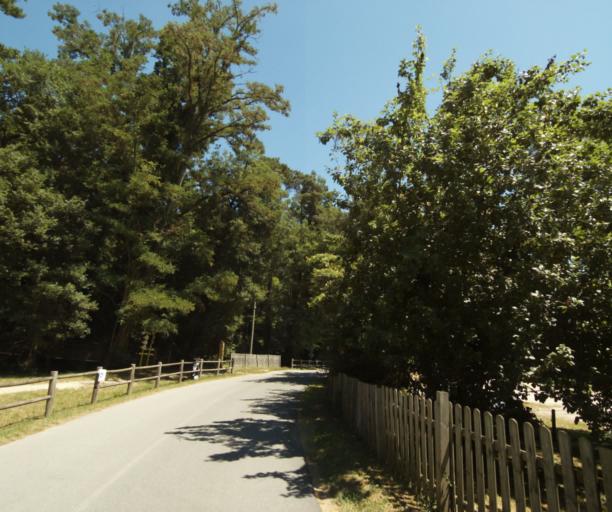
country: FR
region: Centre
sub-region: Departement du Loiret
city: Malesherbes
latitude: 48.2943
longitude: 2.4319
